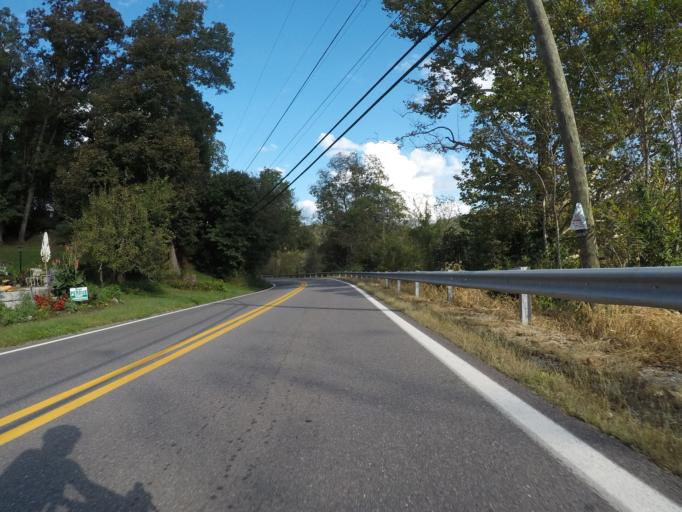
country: US
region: Ohio
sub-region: Lawrence County
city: Burlington
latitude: 38.3844
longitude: -82.5134
